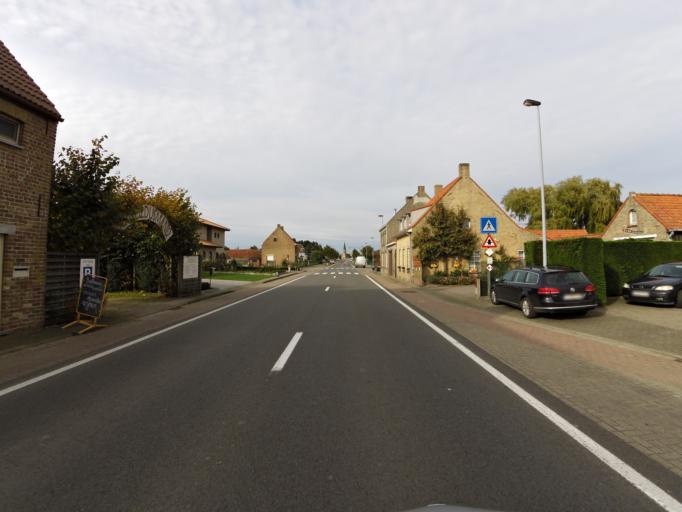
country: BE
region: Flanders
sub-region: Provincie West-Vlaanderen
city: Oudenburg
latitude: 51.1594
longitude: 3.0190
